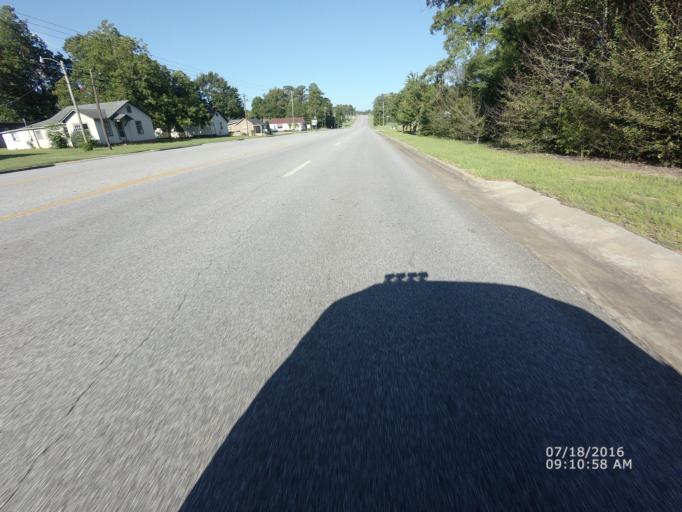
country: US
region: Alabama
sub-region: Chambers County
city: Lanett
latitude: 32.8507
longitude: -85.2060
